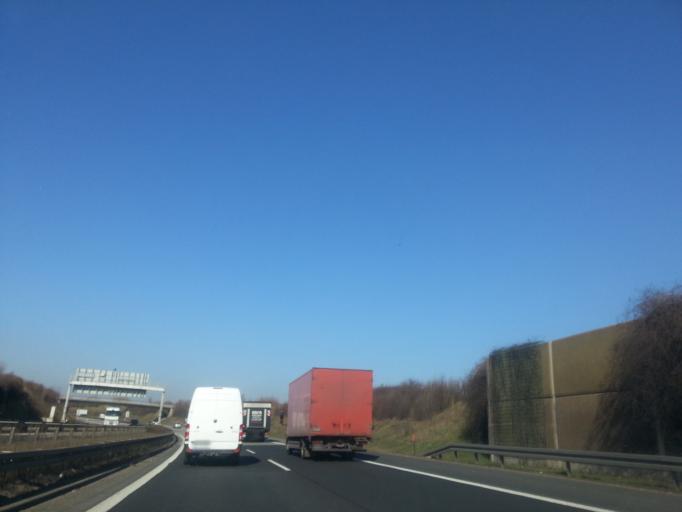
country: DE
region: Saxony
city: Freital
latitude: 51.0452
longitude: 13.6078
